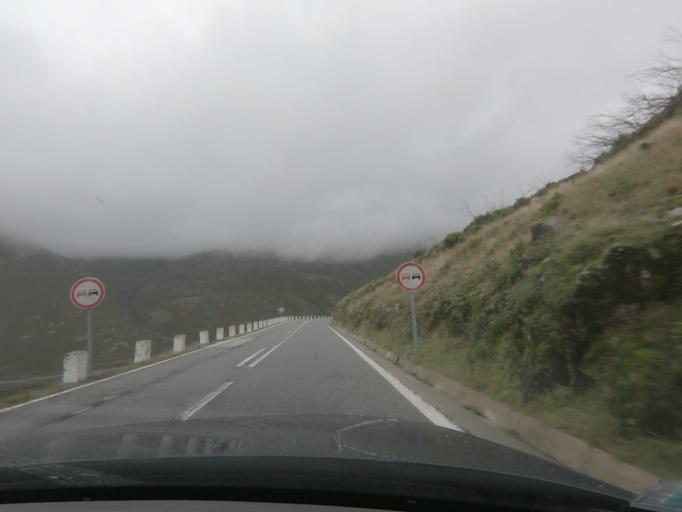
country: PT
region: Vila Real
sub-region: Mondim de Basto
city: Mondim de Basto
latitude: 41.3369
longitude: -7.8713
